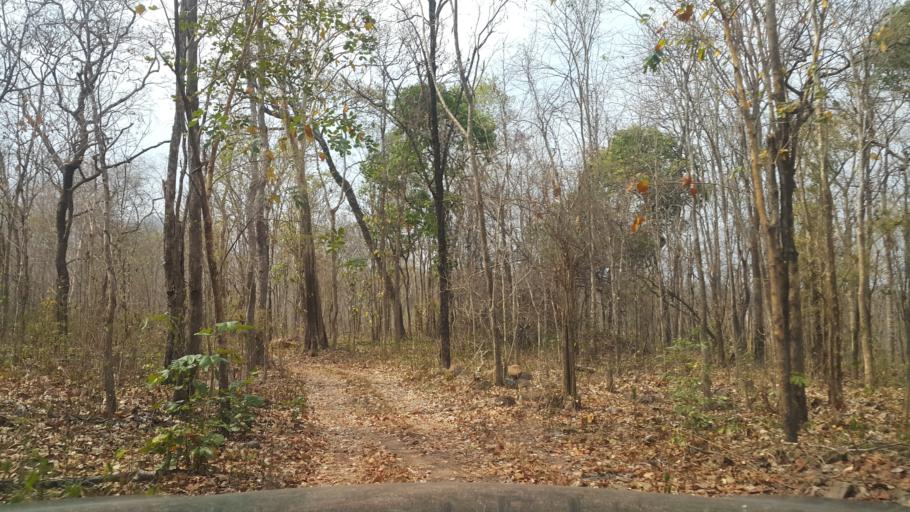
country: TH
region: Lampang
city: Sop Prap
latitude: 17.9311
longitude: 99.2374
